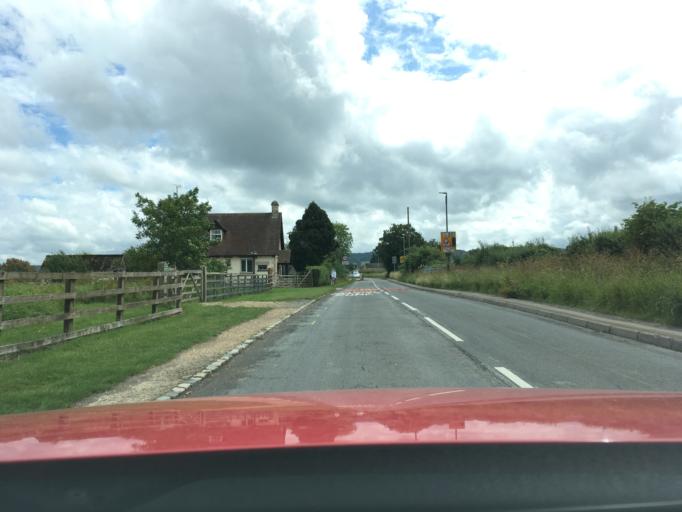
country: GB
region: England
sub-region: Gloucestershire
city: Winchcombe
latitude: 51.9651
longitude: -1.9650
